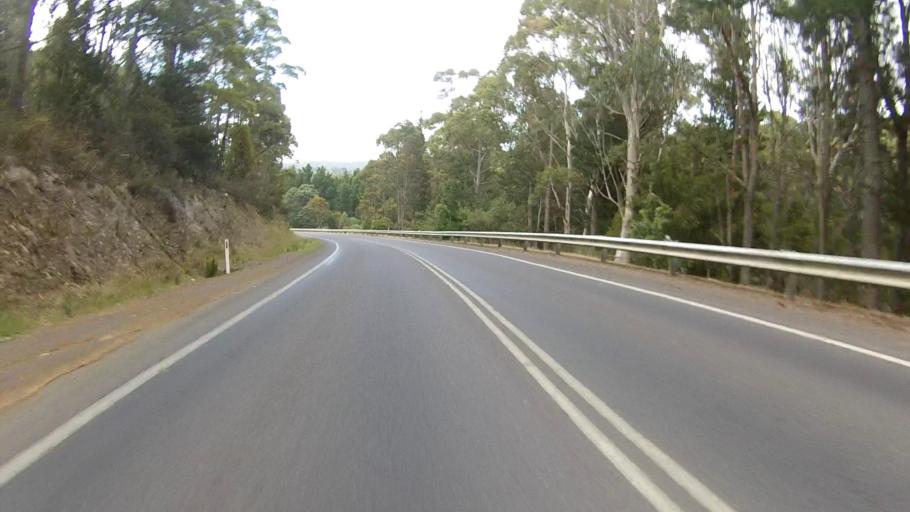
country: AU
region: Tasmania
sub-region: Kingborough
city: Kettering
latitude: -43.0963
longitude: 147.2424
